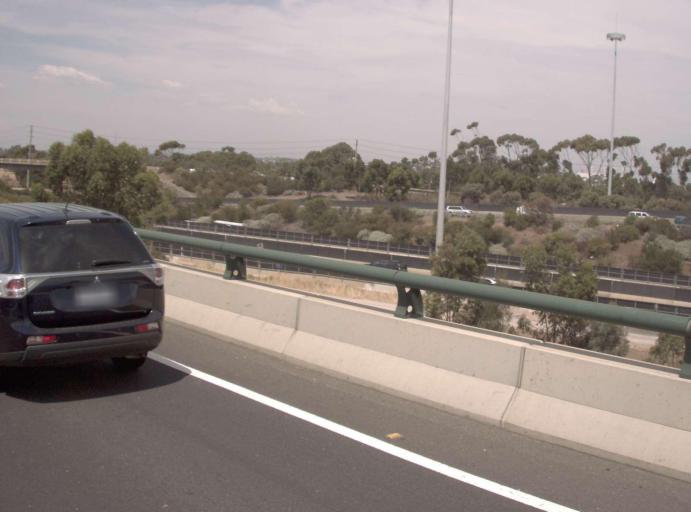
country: AU
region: Victoria
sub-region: Brimbank
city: Brooklyn
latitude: -37.8259
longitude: 144.8190
